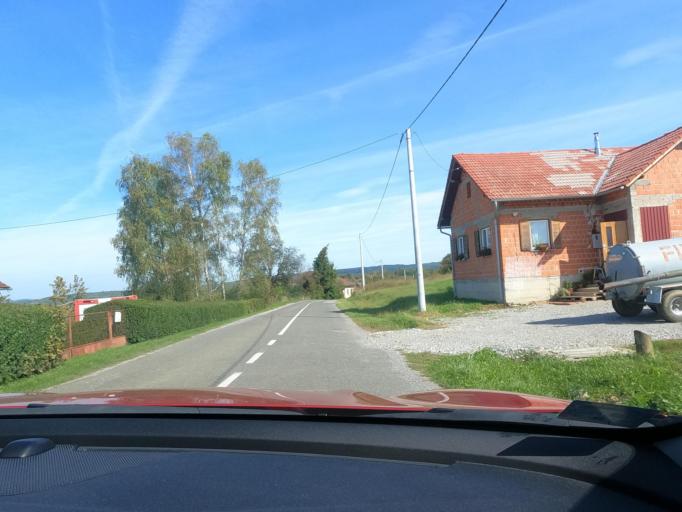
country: HR
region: Sisacko-Moslavacka
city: Petrinja
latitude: 45.3458
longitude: 16.2486
